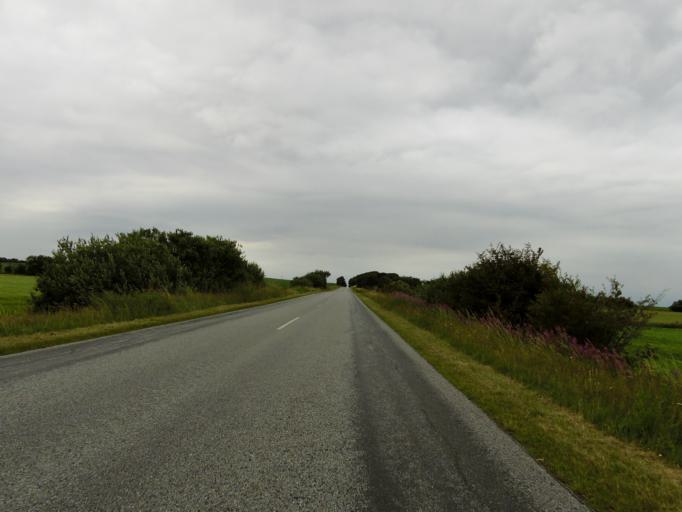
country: DK
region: South Denmark
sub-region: Tonder Kommune
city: Logumkloster
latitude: 55.1337
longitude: 8.9677
